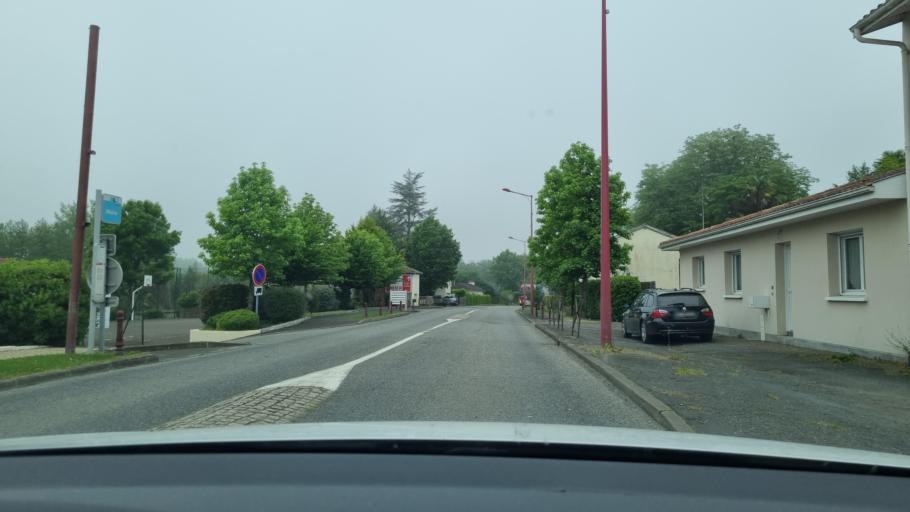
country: FR
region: Aquitaine
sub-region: Departement des Landes
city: Hagetmau
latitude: 43.6148
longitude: -0.6357
